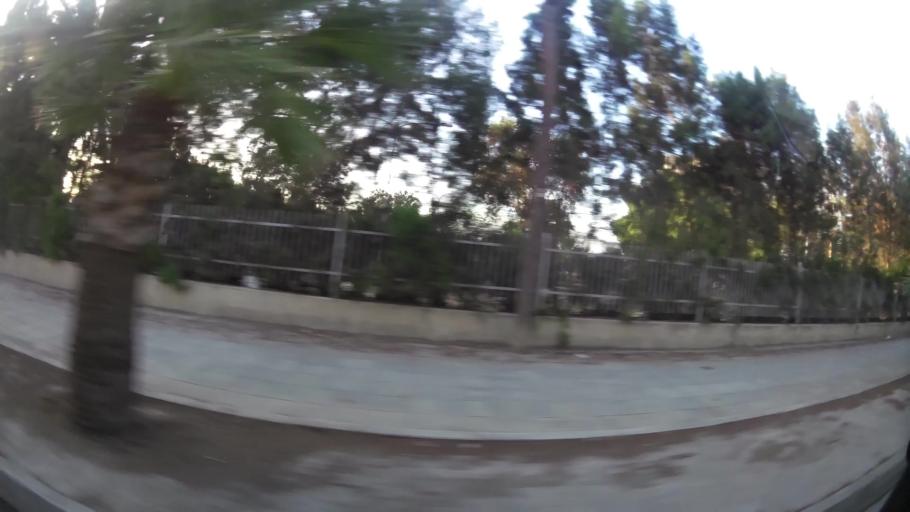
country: CY
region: Larnaka
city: Larnaca
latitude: 34.9222
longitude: 33.6057
